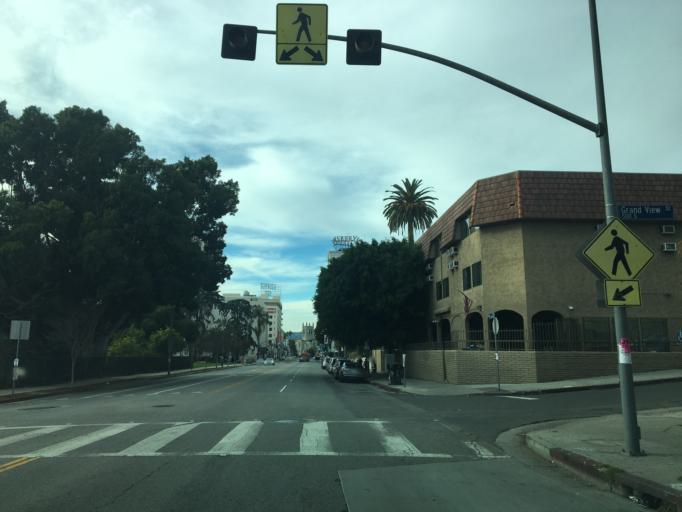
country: US
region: California
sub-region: Los Angeles County
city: Echo Park
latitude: 34.0604
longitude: -118.2768
